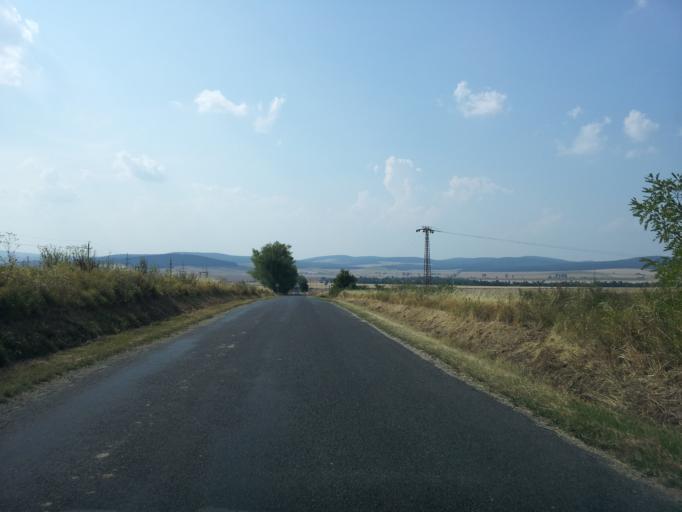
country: HU
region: Veszprem
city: Nemesvamos
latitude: 47.0156
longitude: 17.8110
